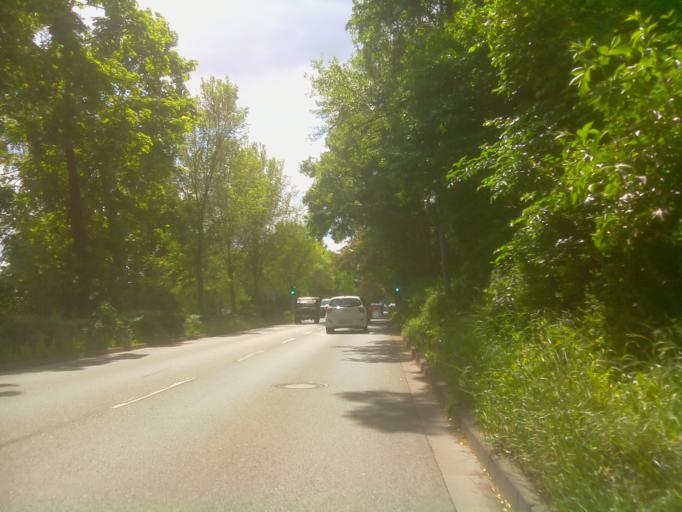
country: DE
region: Rheinland-Pfalz
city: Speyer
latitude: 49.3170
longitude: 8.4462
